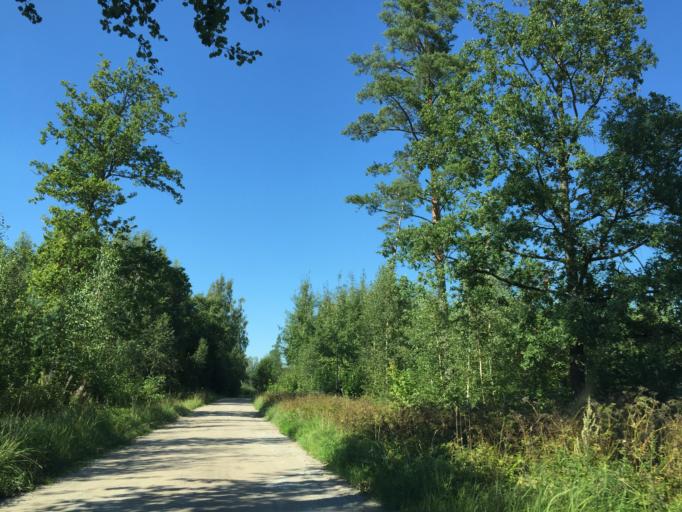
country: LV
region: Limbazu Rajons
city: Limbazi
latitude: 57.5540
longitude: 24.7700
